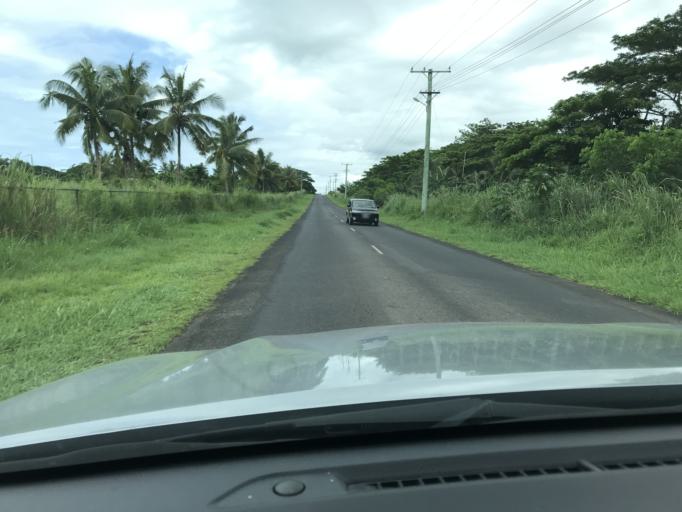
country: WS
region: Aiga-i-le-Tai
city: Mulifanua
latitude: -13.8323
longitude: -172.0295
